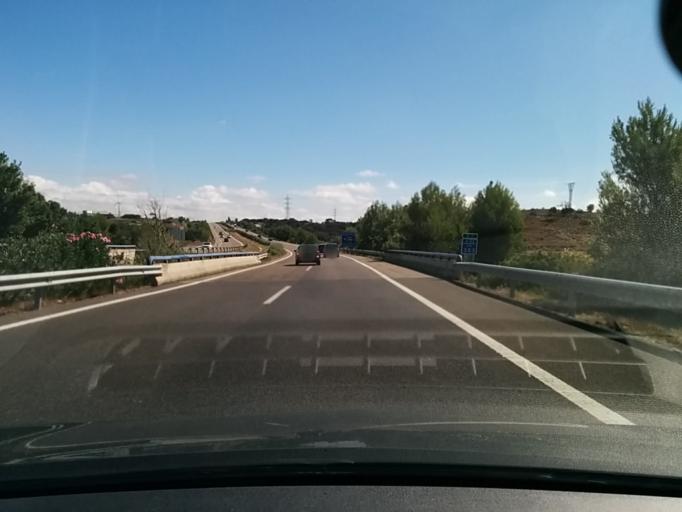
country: ES
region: Aragon
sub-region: Provincia de Huesca
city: Alerre
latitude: 42.0978
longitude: -0.4696
